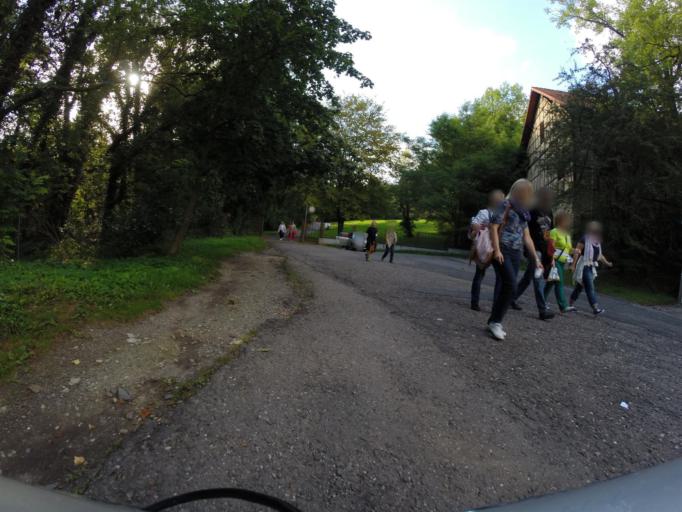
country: DE
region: Thuringia
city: Jena
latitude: 50.9447
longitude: 11.5897
